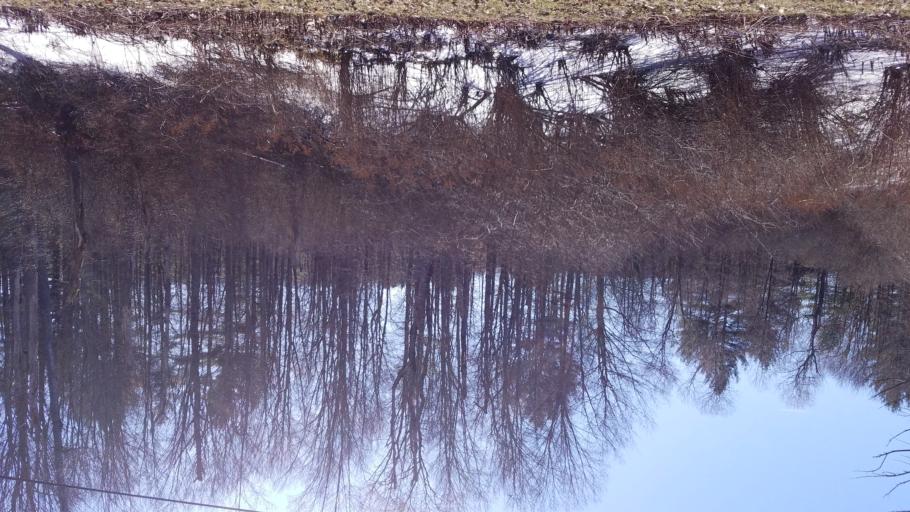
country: US
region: New York
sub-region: Allegany County
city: Wellsville
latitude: 42.0485
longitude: -77.9223
